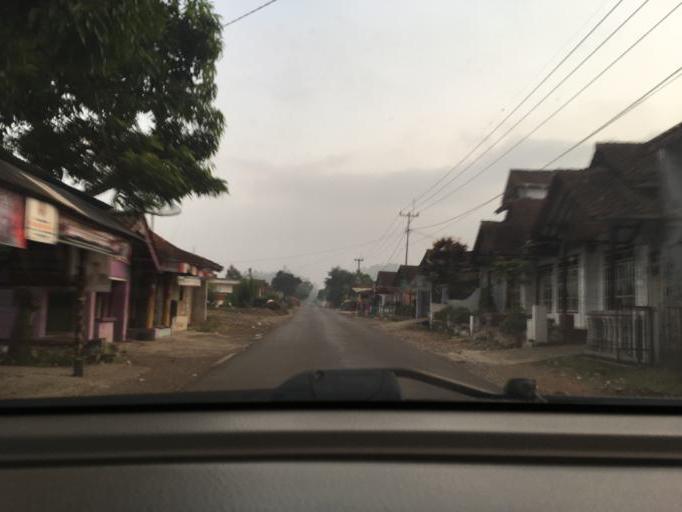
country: ID
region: West Java
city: Pasireurih
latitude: -7.1851
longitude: 108.1970
